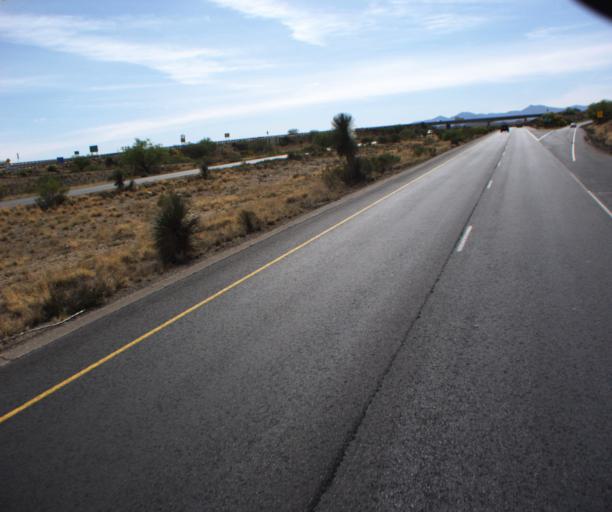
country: US
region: Arizona
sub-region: Pima County
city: Vail
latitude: 32.0092
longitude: -110.6940
